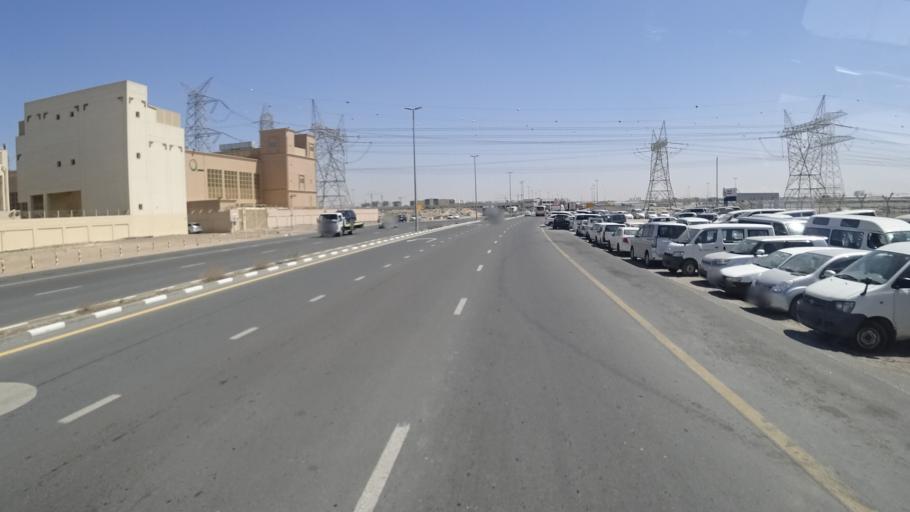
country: AE
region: Ash Shariqah
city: Sharjah
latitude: 25.1742
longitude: 55.3805
